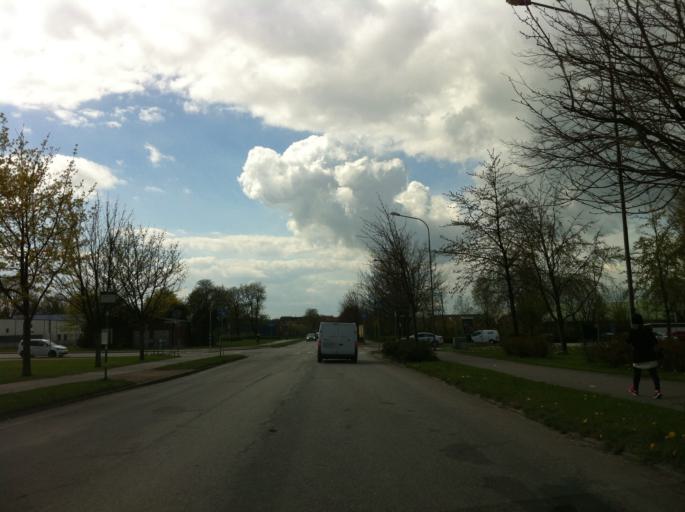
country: SE
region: Skane
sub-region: Eslovs Kommun
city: Eslov
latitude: 55.8402
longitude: 13.3171
